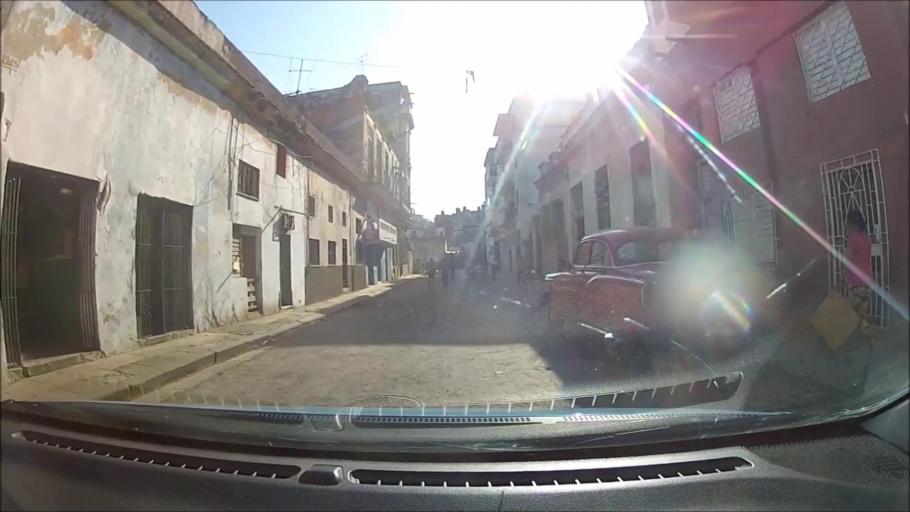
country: CU
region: La Habana
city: Centro Habana
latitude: 23.1386
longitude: -82.3624
